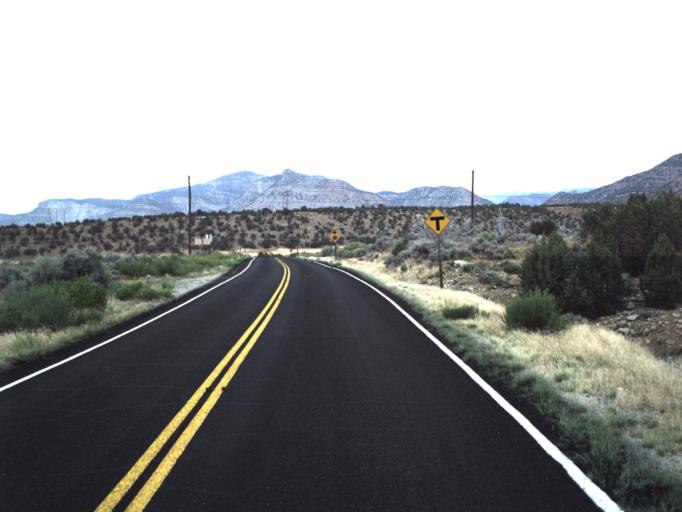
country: US
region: Utah
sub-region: Carbon County
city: East Carbon City
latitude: 39.5165
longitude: -110.3921
